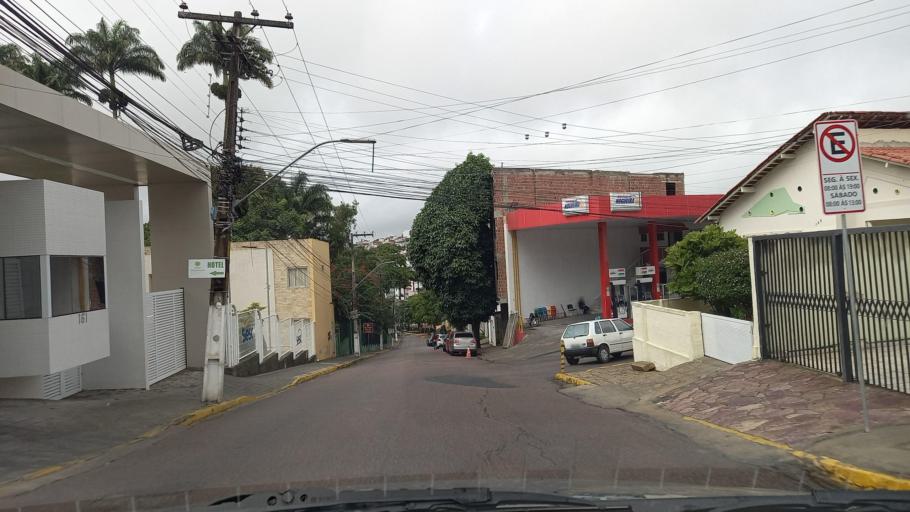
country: BR
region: Pernambuco
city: Garanhuns
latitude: -8.8922
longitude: -36.4918
